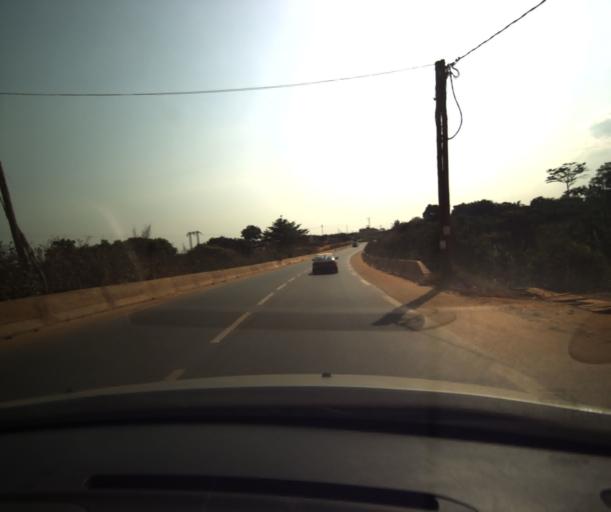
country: CM
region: Centre
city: Okoa
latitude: 3.9625
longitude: 11.5388
